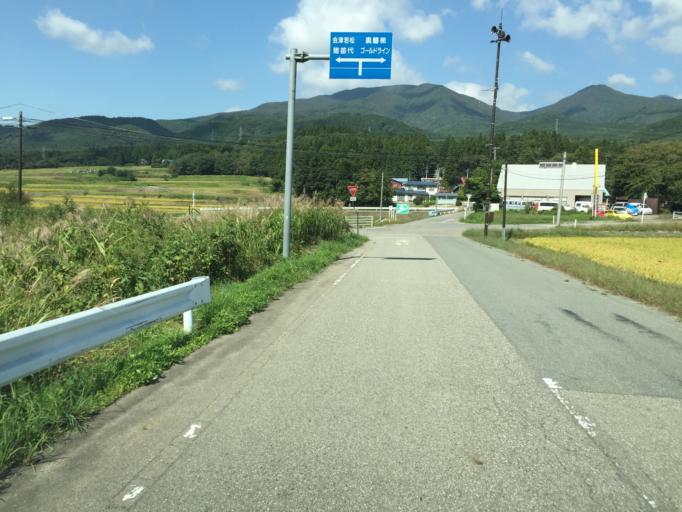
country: JP
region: Fukushima
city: Inawashiro
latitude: 37.5618
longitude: 140.0045
